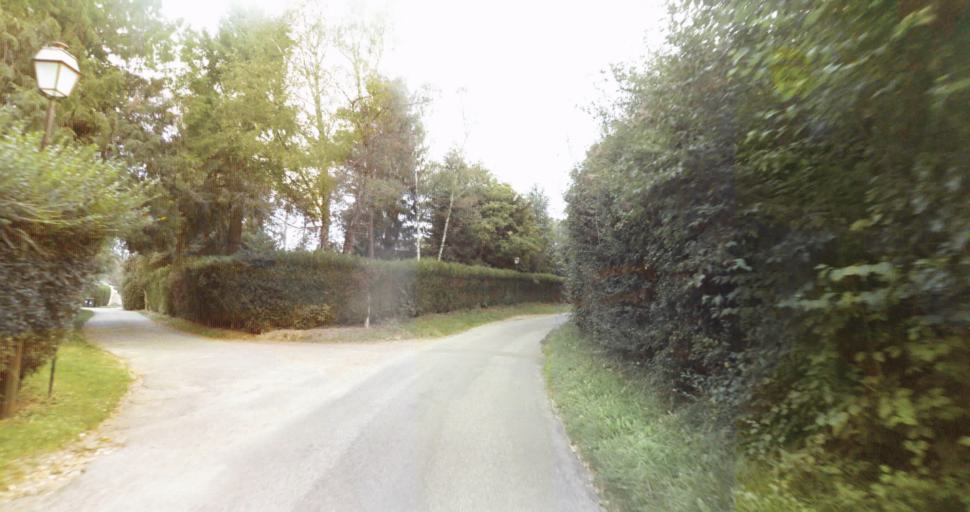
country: FR
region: Centre
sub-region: Departement d'Eure-et-Loir
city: Sorel-Moussel
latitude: 48.8600
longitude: 1.3457
